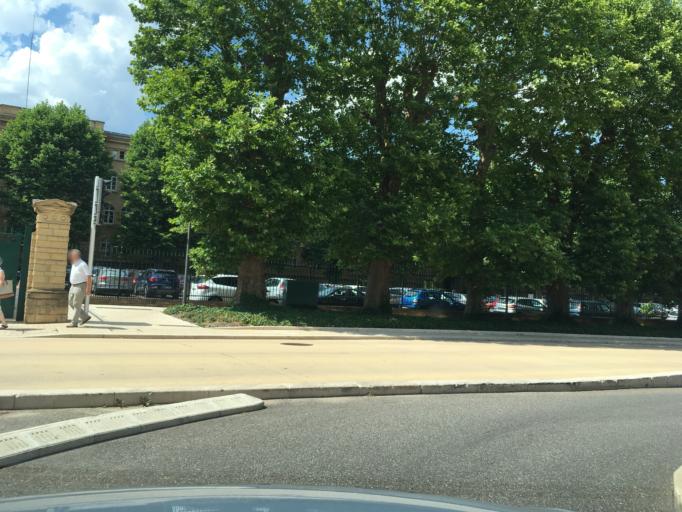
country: FR
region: Lorraine
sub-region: Departement de la Moselle
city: Metz
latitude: 49.1252
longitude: 6.1739
